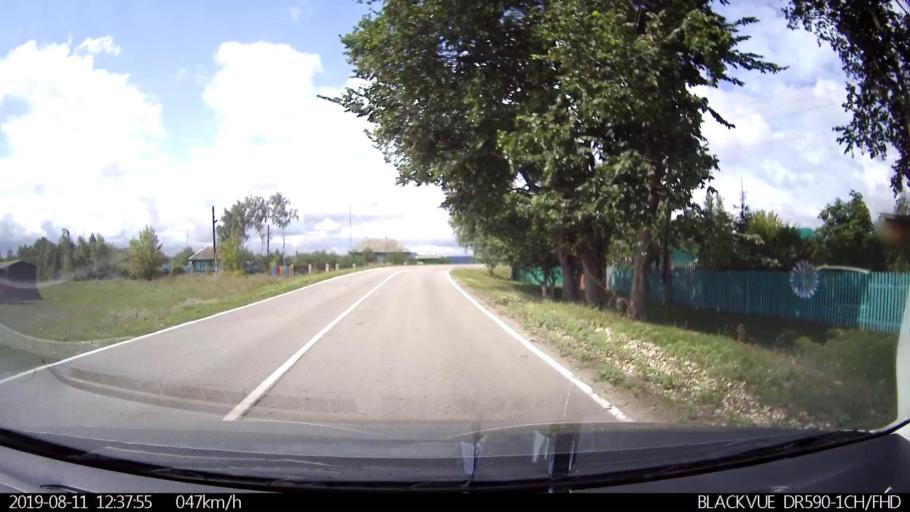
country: RU
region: Ulyanovsk
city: Ignatovka
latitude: 53.8244
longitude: 47.8096
